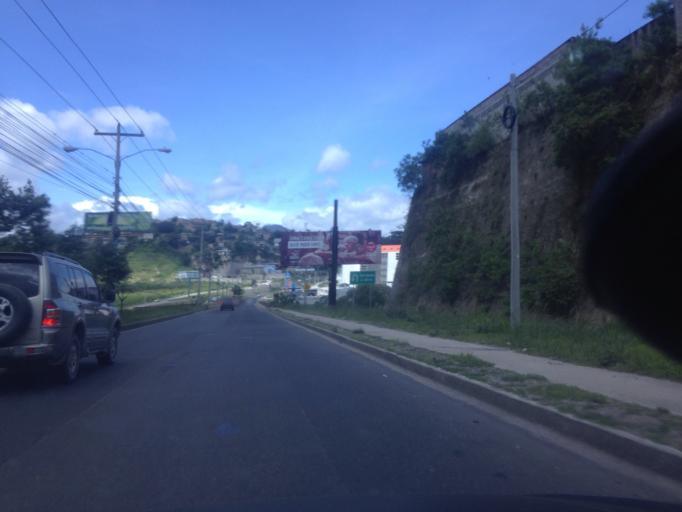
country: HN
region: Francisco Morazan
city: Tegucigalpa
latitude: 14.0507
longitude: -87.2077
